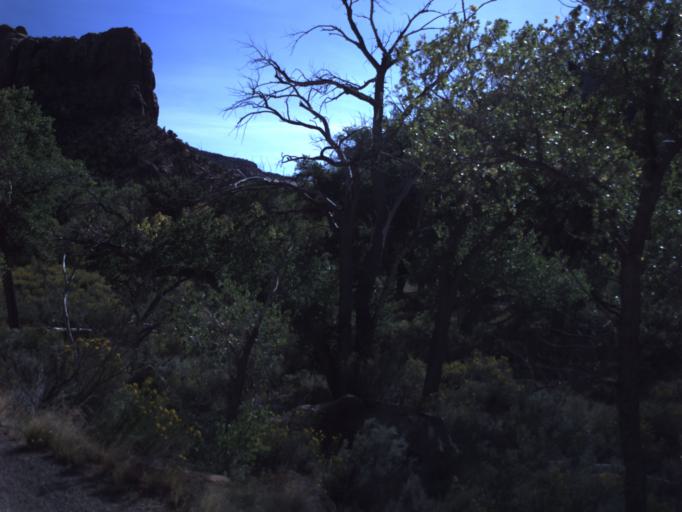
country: US
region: Utah
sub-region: San Juan County
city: Monticello
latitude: 38.0400
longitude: -109.5533
